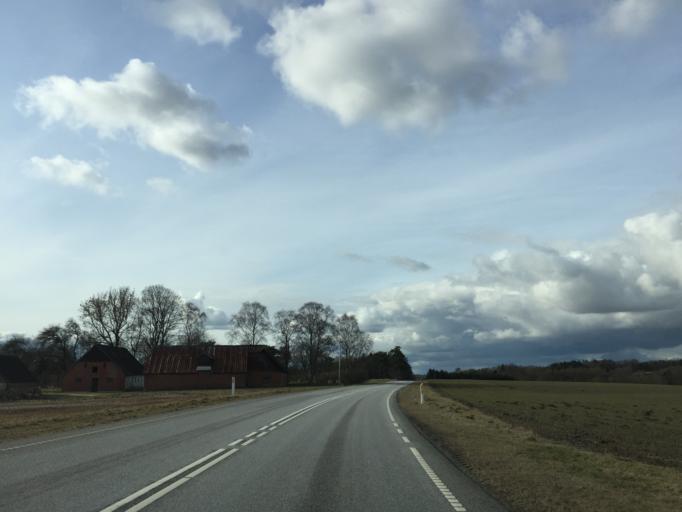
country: DK
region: Central Jutland
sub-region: Favrskov Kommune
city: Hammel
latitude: 56.2107
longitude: 9.7809
